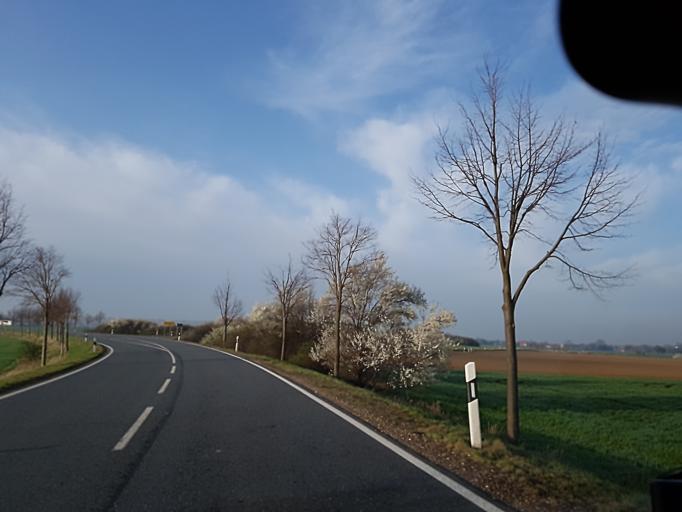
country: DE
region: Saxony
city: Strehla
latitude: 51.3611
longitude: 13.2619
